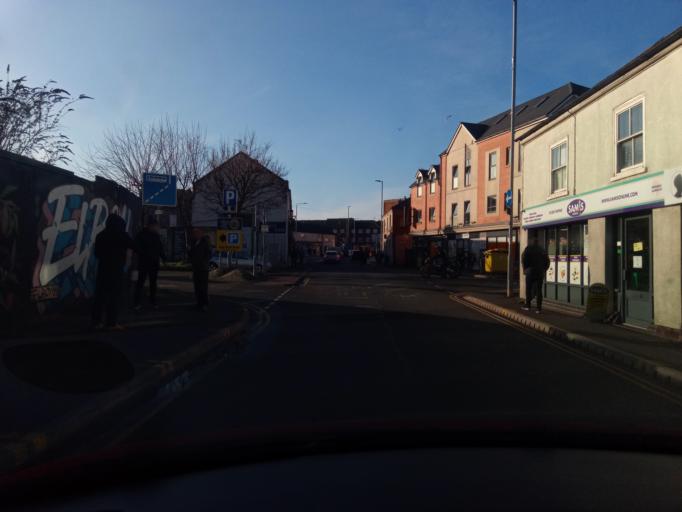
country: GB
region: England
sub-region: Leicestershire
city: Loughborough
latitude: 52.7724
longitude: -1.2083
